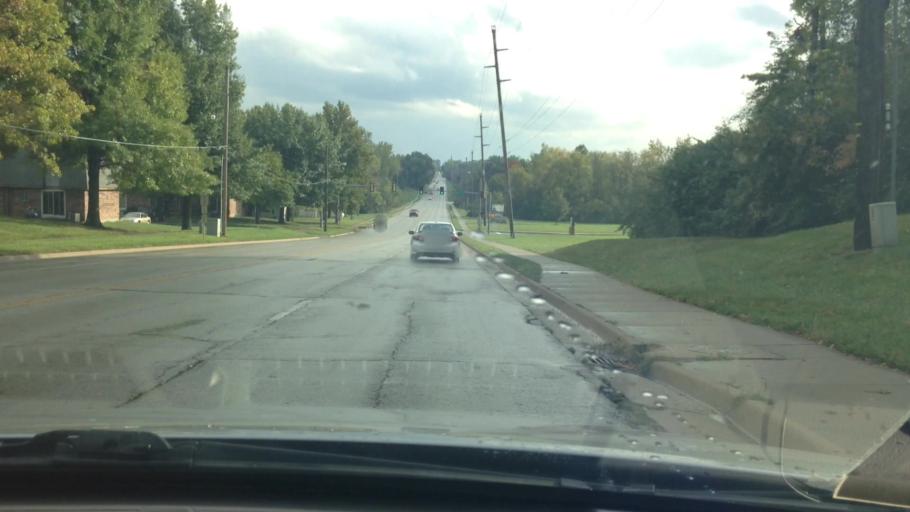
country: US
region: Kansas
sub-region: Leavenworth County
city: Leavenworth
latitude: 39.2839
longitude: -94.9279
